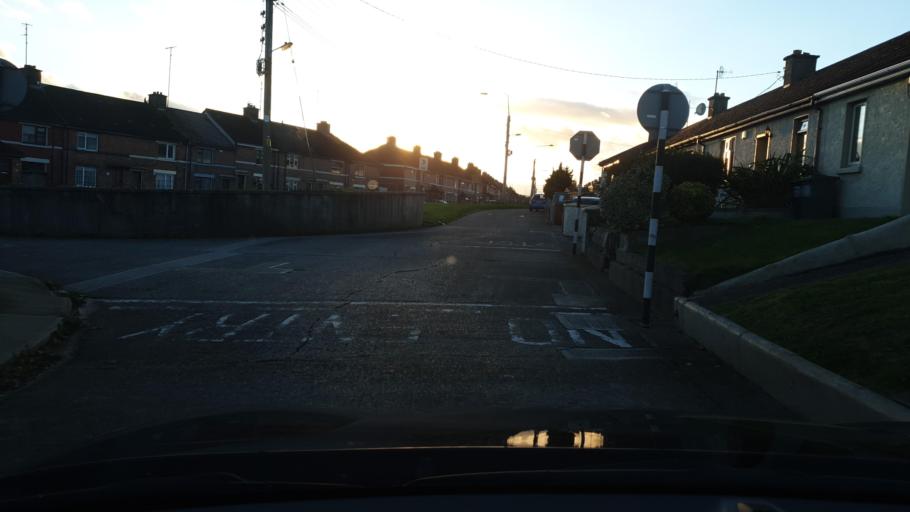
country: IE
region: Leinster
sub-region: Lu
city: Drogheda
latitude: 53.7214
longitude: -6.3420
